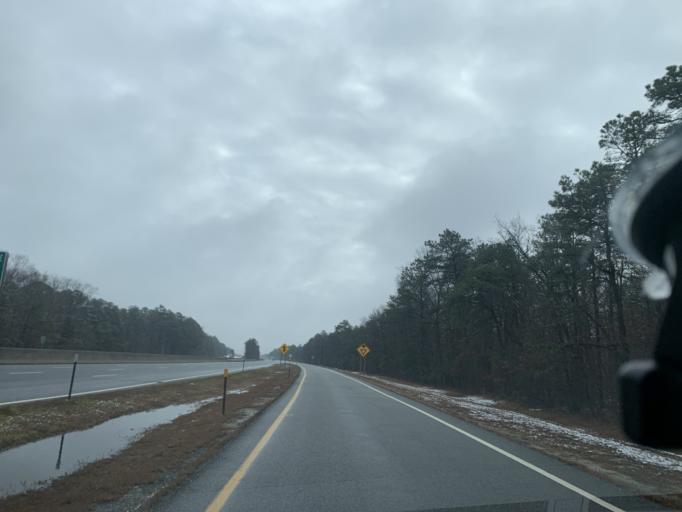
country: US
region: New Jersey
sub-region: Atlantic County
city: Pomona
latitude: 39.4457
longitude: -74.6187
